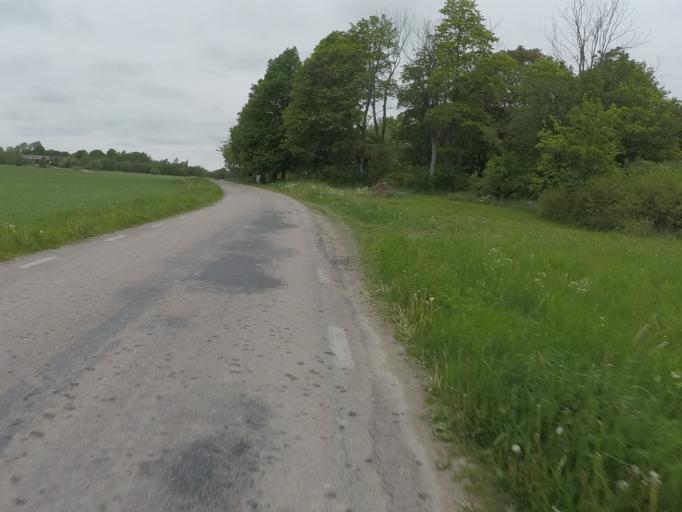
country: SE
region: Vaestmanland
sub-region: Hallstahammars Kommun
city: Kolback
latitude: 59.5474
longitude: 16.2962
